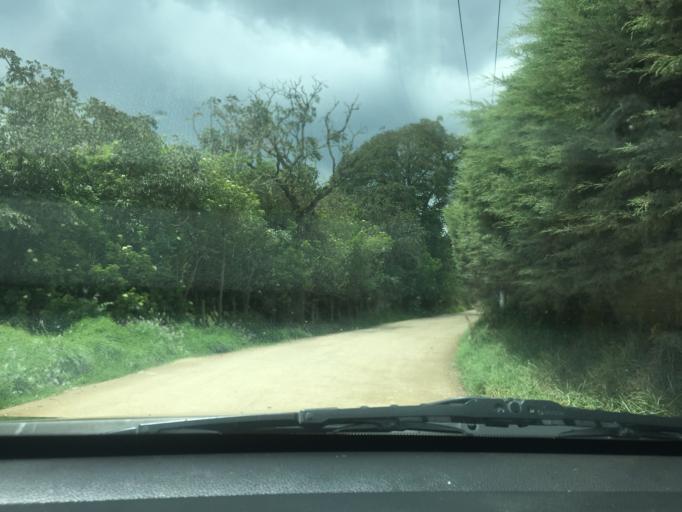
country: CO
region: Cundinamarca
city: Facatativa
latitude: 4.8007
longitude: -74.3049
